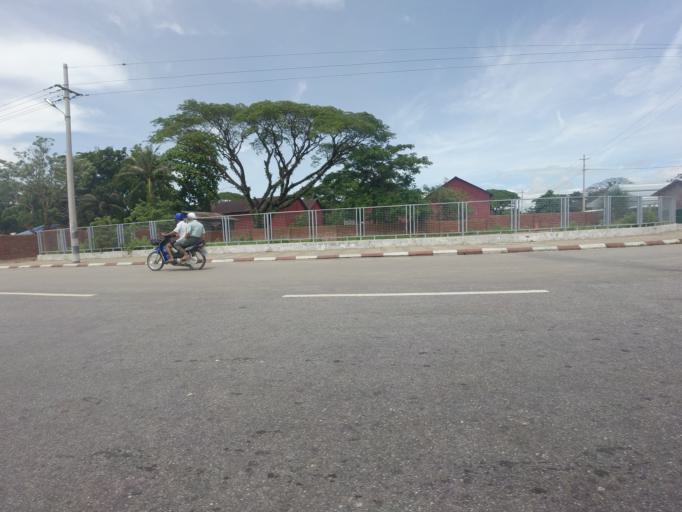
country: MM
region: Mon
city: Mawlamyine
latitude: 16.4520
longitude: 97.6227
